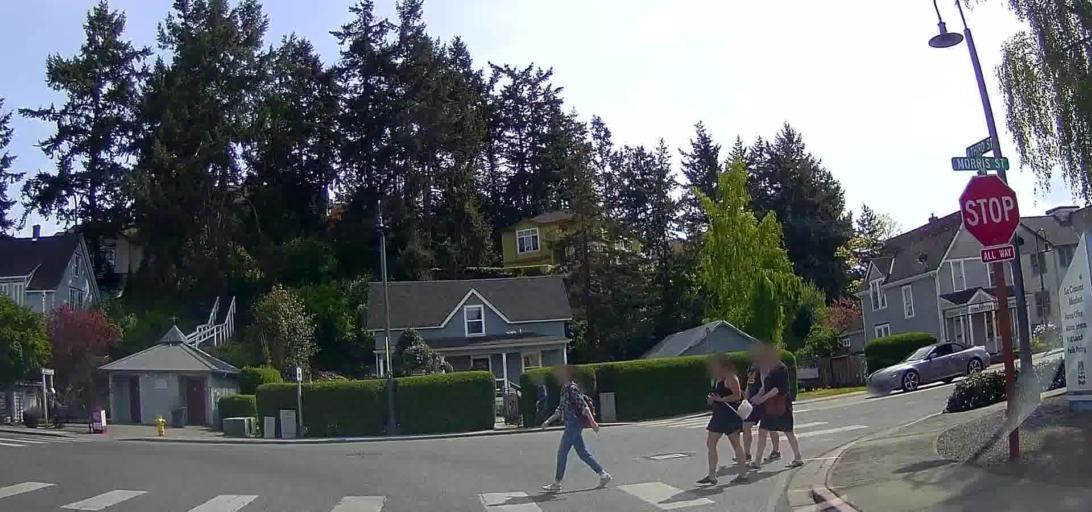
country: US
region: Washington
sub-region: Skagit County
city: Mount Vernon
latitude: 48.3923
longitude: -122.4940
